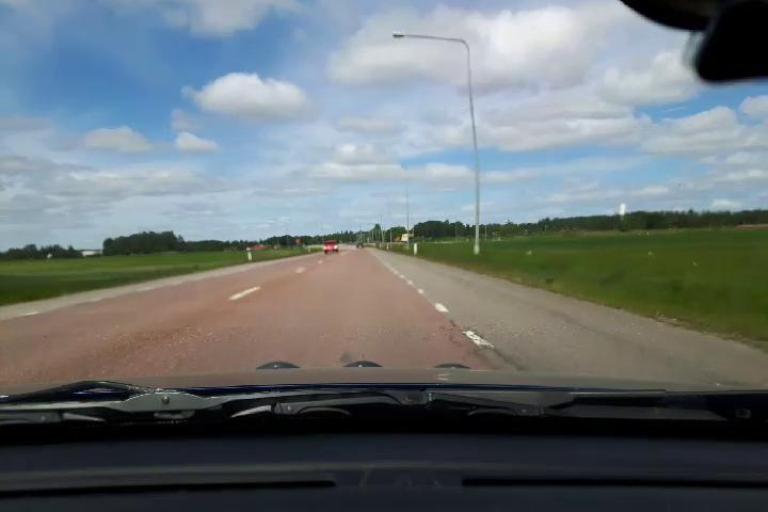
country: SE
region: Uppsala
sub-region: Osthammars Kommun
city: Bjorklinge
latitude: 60.0158
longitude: 17.5577
